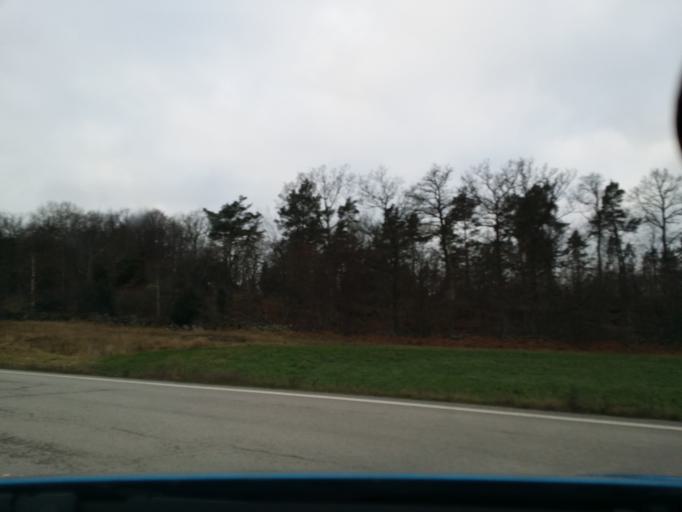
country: SE
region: Blekinge
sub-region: Karlshamns Kommun
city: Morrum
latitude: 56.1786
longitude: 14.7294
